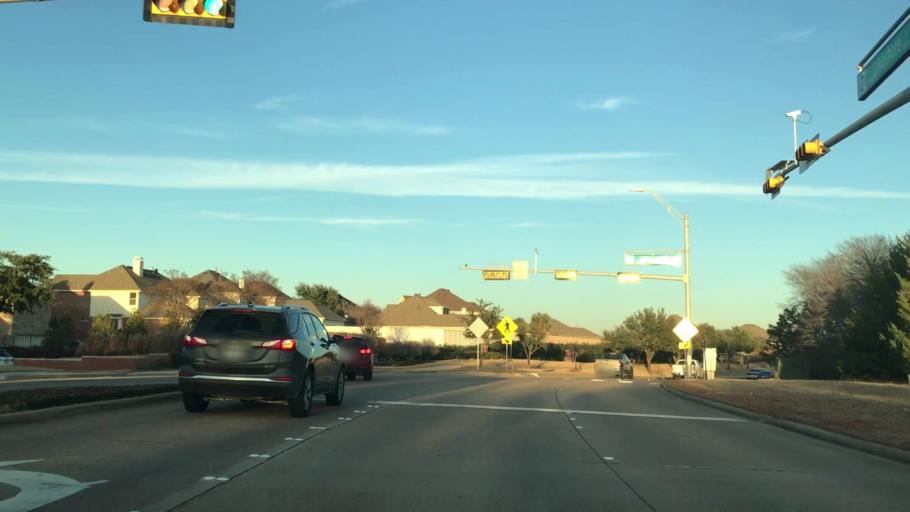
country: US
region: Texas
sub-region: Rockwall County
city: Rockwall
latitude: 32.9448
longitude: -96.4749
